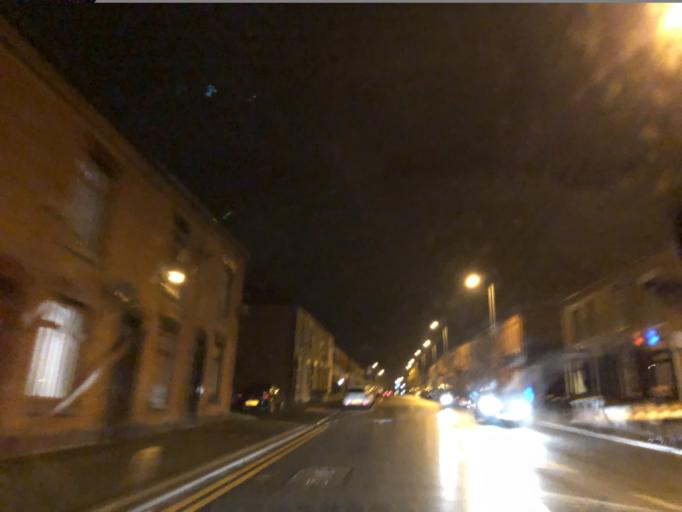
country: GB
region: England
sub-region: Borough of Oldham
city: Shaw
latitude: 53.5549
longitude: -2.0833
